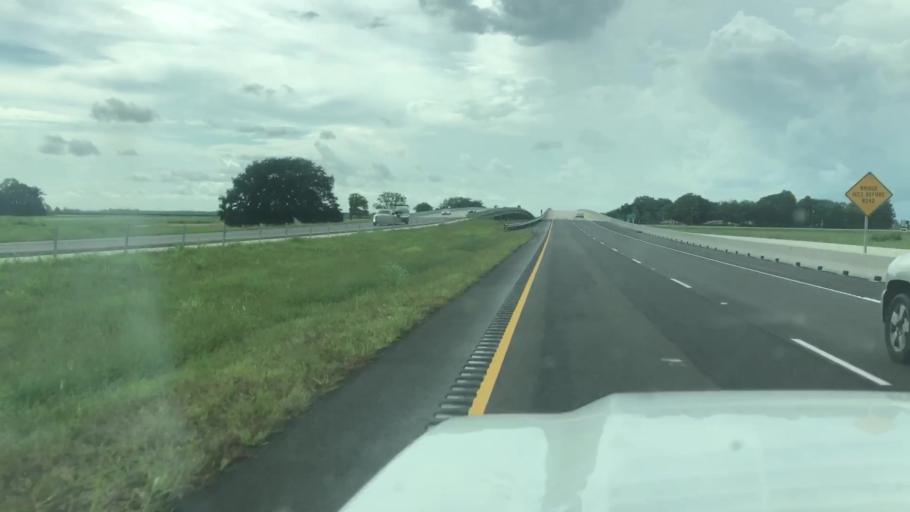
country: US
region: Louisiana
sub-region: Iberia Parish
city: Jeanerette
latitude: 29.8646
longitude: -91.6294
